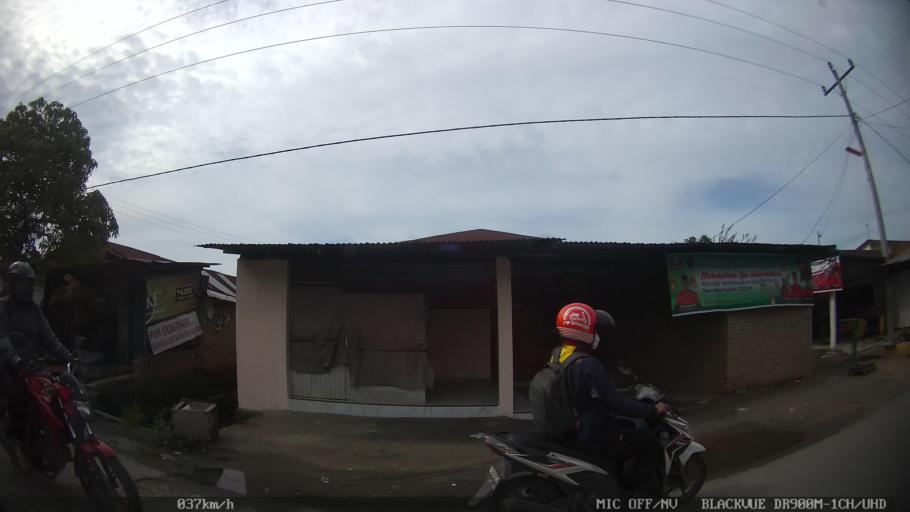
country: ID
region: North Sumatra
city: Medan
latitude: 3.6212
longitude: 98.7116
